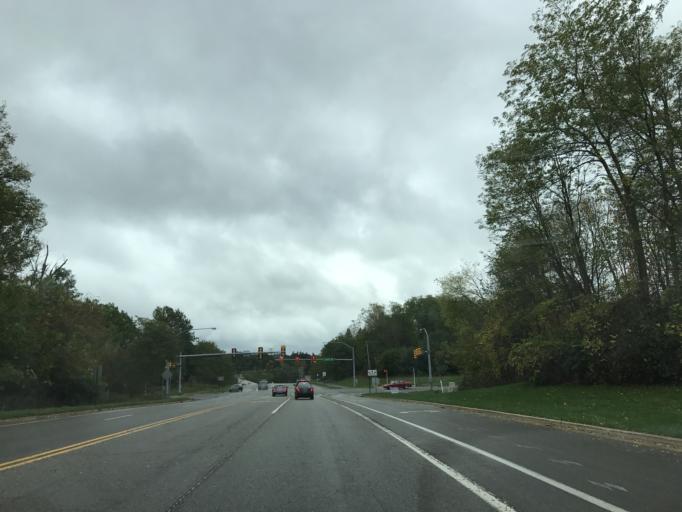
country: US
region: Michigan
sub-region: Washtenaw County
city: Ypsilanti
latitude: 42.2753
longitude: -83.6713
